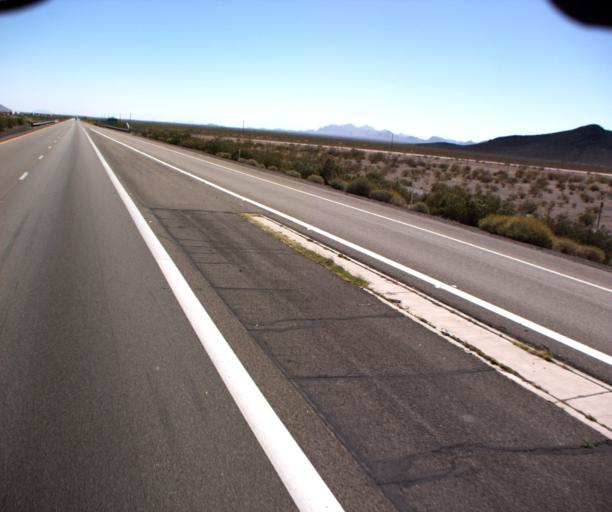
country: US
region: Arizona
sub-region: La Paz County
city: Salome
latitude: 33.6082
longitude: -113.6161
